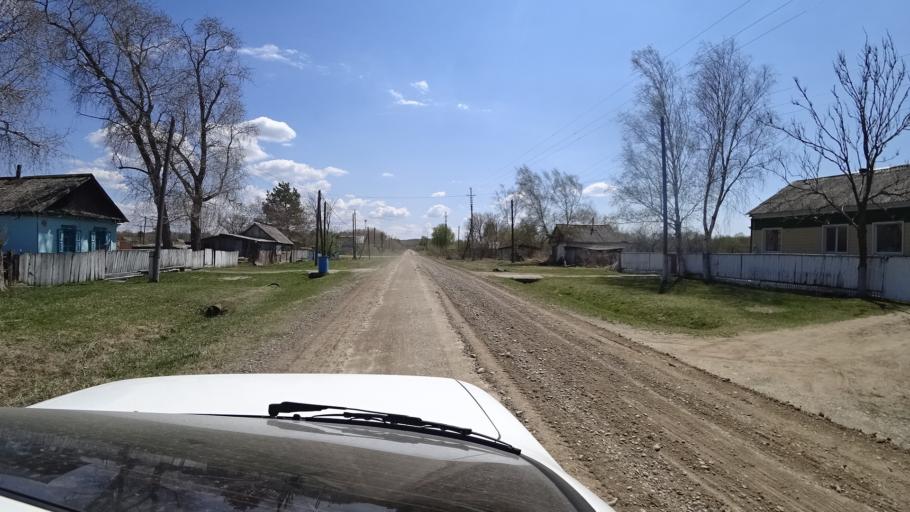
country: RU
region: Primorskiy
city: Lazo
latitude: 45.7993
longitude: 133.7637
